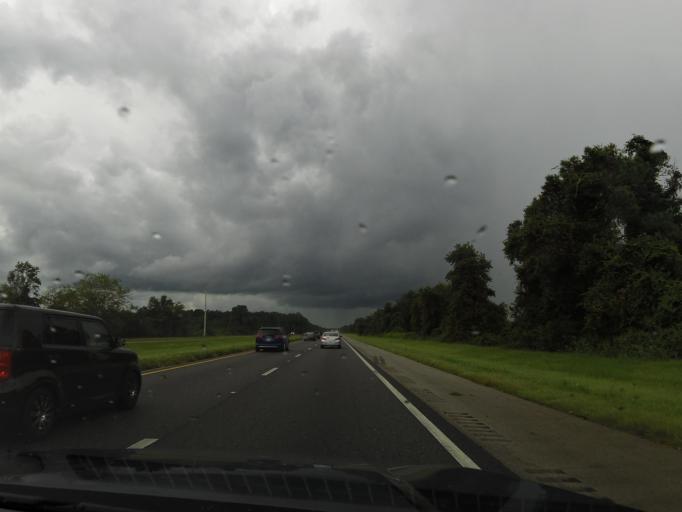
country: US
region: Florida
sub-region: Duval County
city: Baldwin
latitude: 30.2994
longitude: -81.9331
